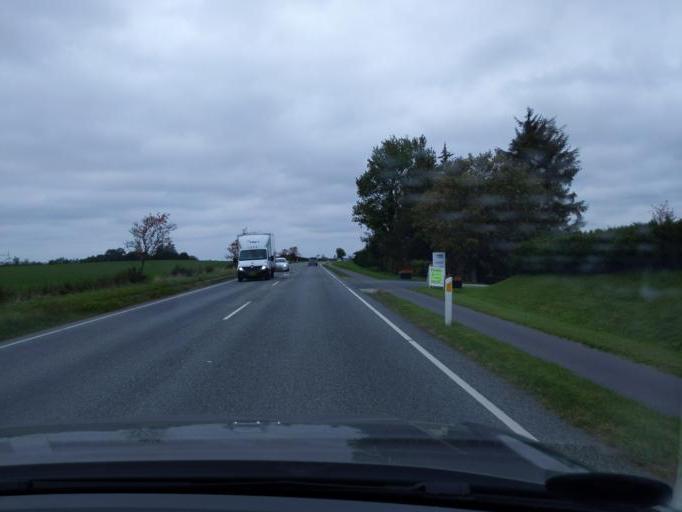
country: DK
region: Central Jutland
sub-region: Randers Kommune
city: Randers
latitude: 56.4989
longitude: 9.9672
